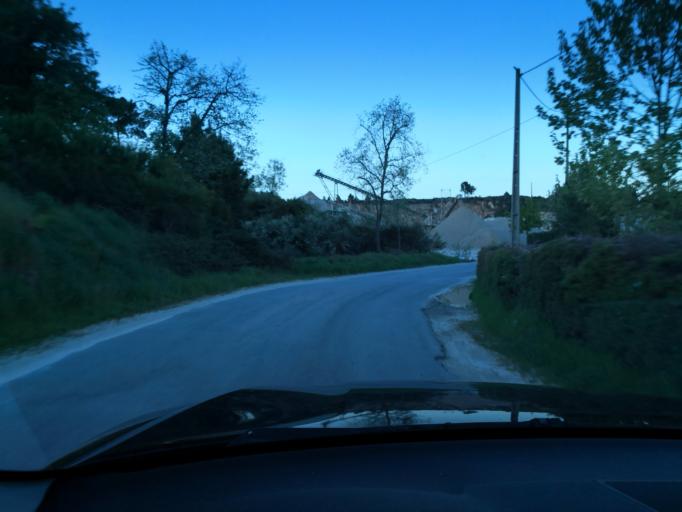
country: PT
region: Vila Real
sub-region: Vila Real
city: Vila Real
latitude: 41.3447
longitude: -7.6948
